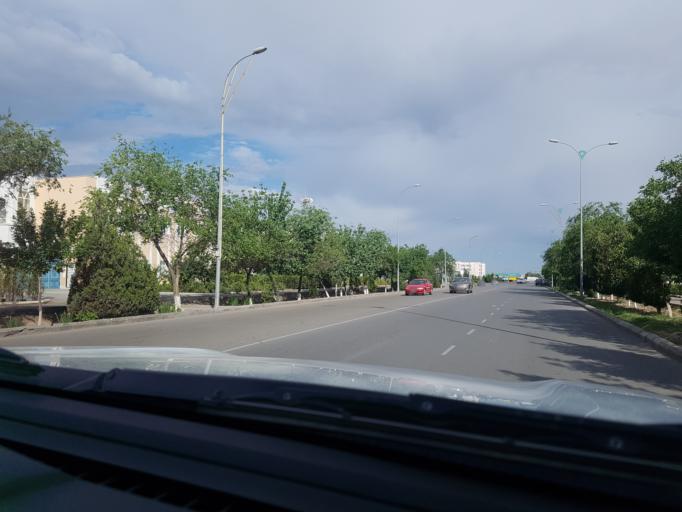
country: TM
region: Dasoguz
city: Dasoguz
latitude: 41.8443
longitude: 59.9348
